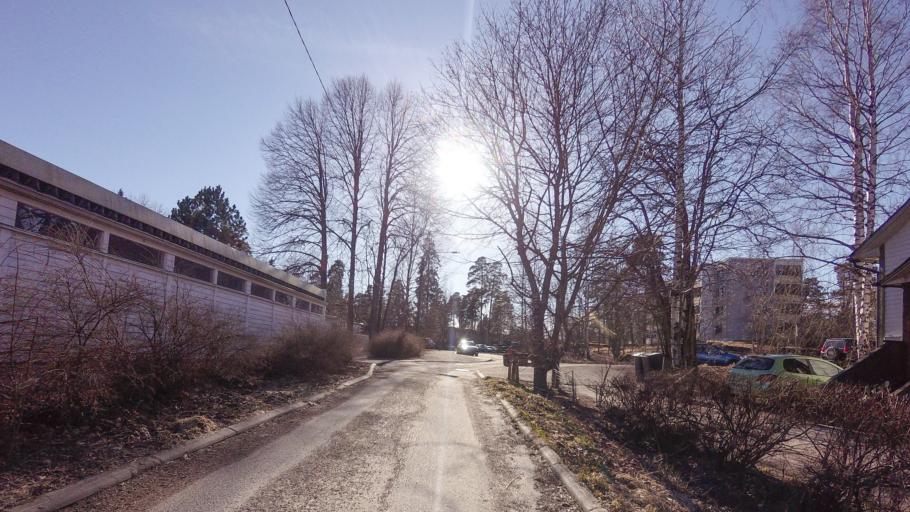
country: FI
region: Uusimaa
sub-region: Helsinki
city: Vantaa
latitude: 60.1799
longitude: 25.0632
